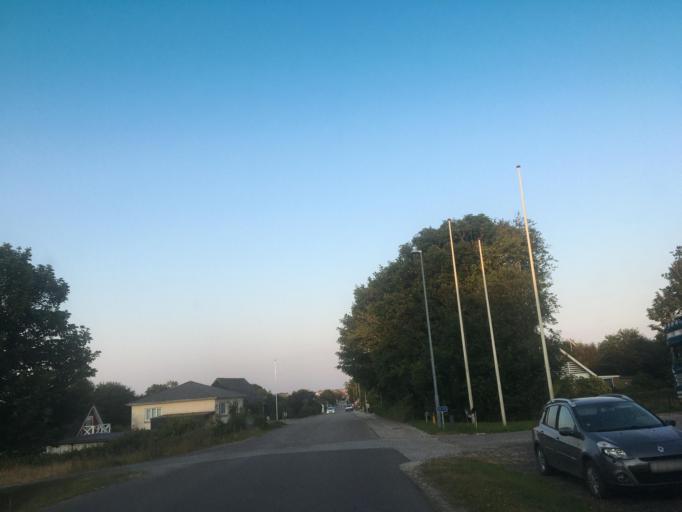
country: DK
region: North Denmark
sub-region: Thisted Kommune
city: Hurup
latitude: 56.7516
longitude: 8.4016
